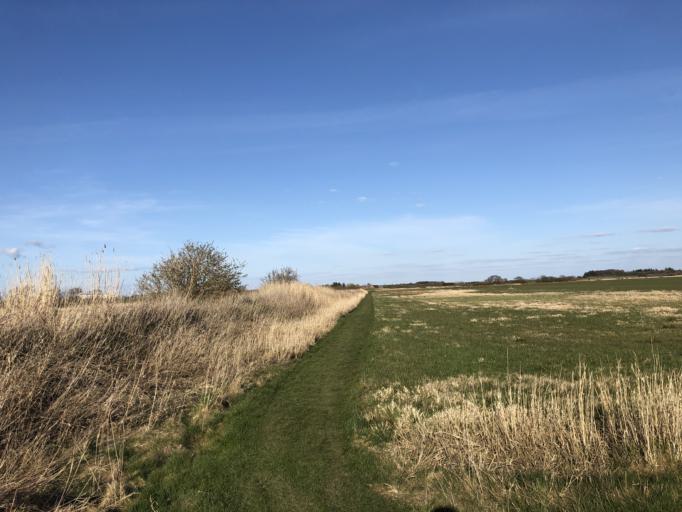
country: DK
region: Central Jutland
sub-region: Holstebro Kommune
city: Ulfborg
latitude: 56.3306
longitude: 8.3129
